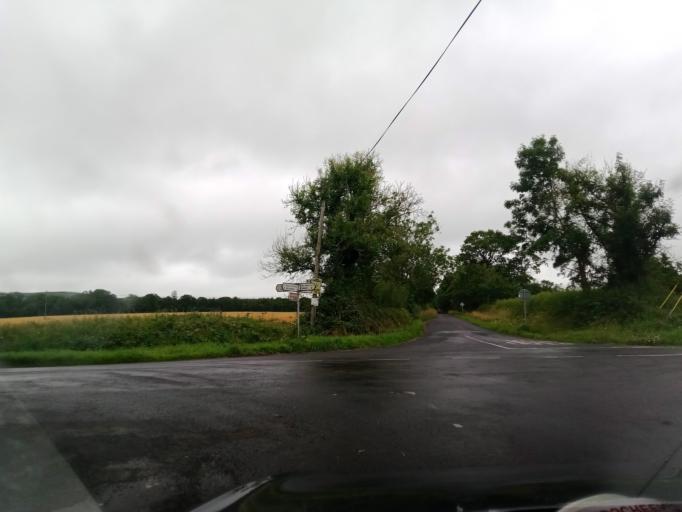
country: IE
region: Leinster
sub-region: Laois
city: Abbeyleix
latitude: 52.9306
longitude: -7.2751
